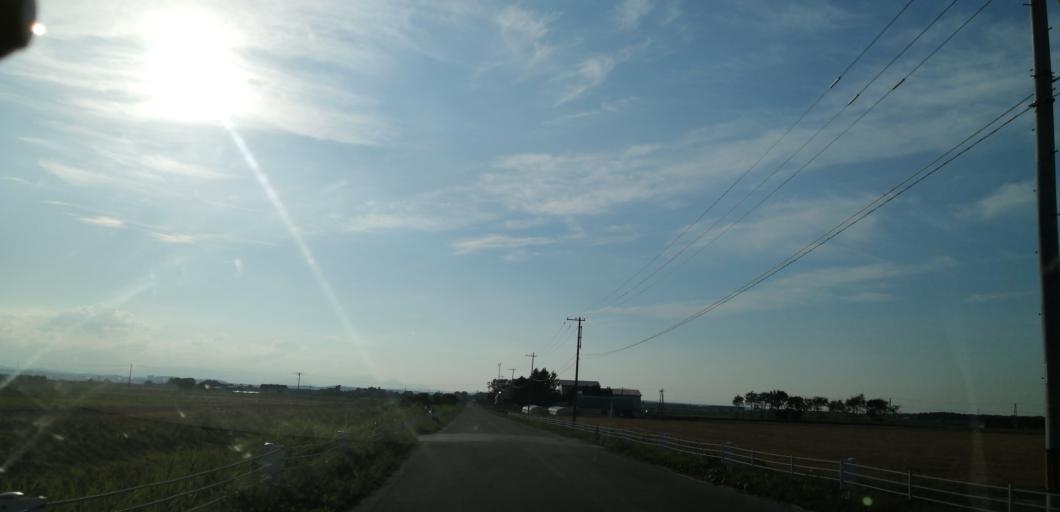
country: JP
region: Hokkaido
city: Kitahiroshima
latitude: 42.9566
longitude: 141.6532
